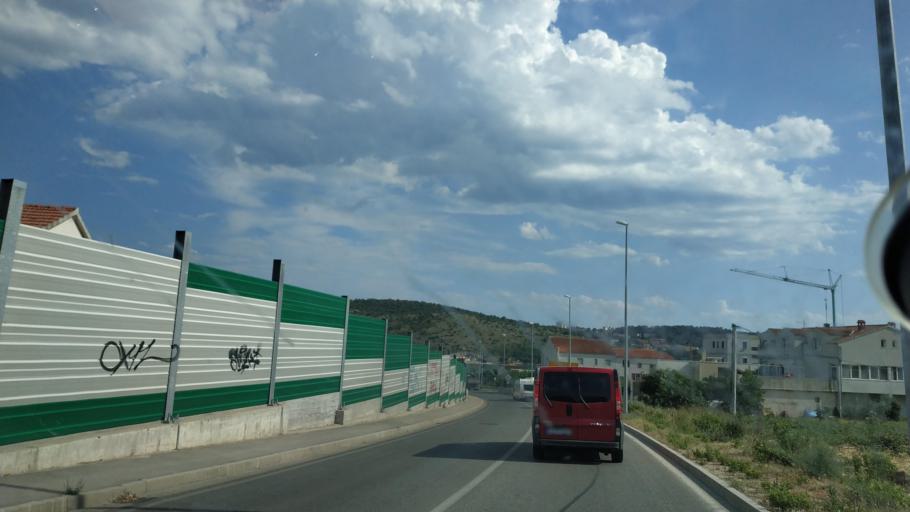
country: HR
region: Splitsko-Dalmatinska
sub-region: Grad Trogir
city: Trogir
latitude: 43.5261
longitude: 16.2633
